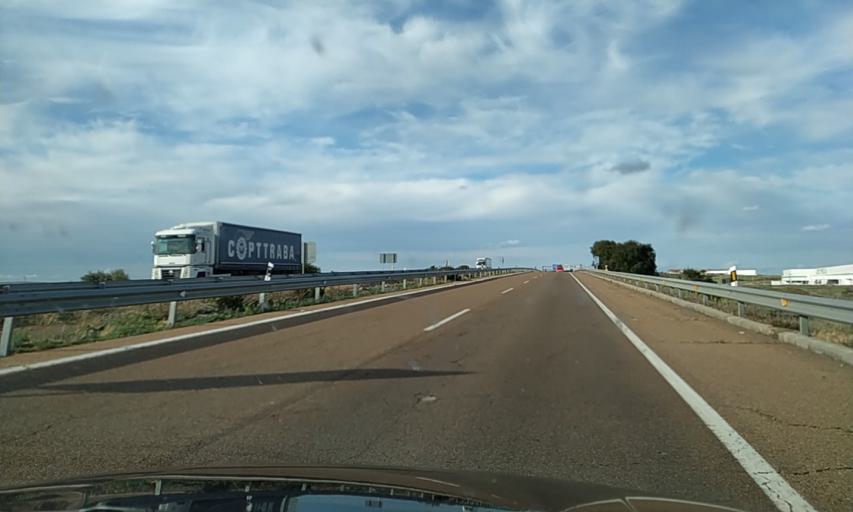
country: ES
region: Extremadura
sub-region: Provincia de Badajoz
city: Badajoz
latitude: 38.8999
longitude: -7.0019
